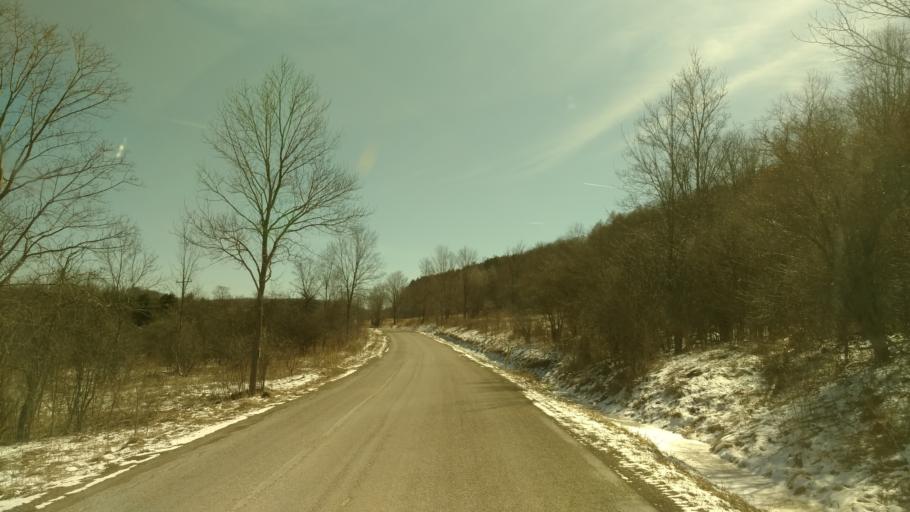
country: US
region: New York
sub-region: Allegany County
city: Andover
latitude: 41.9291
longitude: -77.7980
